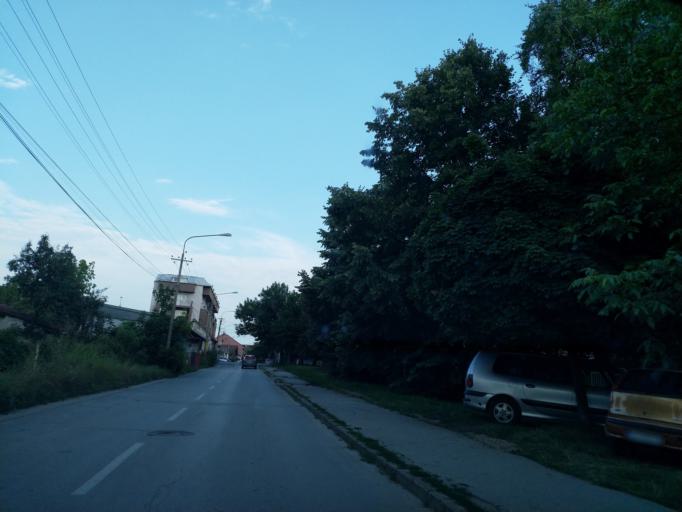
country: RS
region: Central Serbia
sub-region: Pomoravski Okrug
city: Jagodina
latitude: 43.9737
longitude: 21.2539
